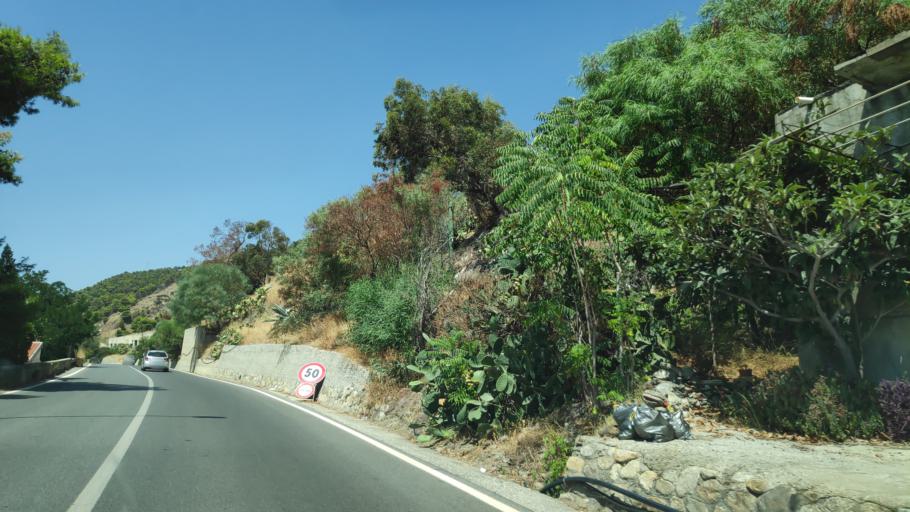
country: IT
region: Calabria
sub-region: Provincia di Reggio Calabria
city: Palizzi Marina
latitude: 37.9200
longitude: 15.9762
